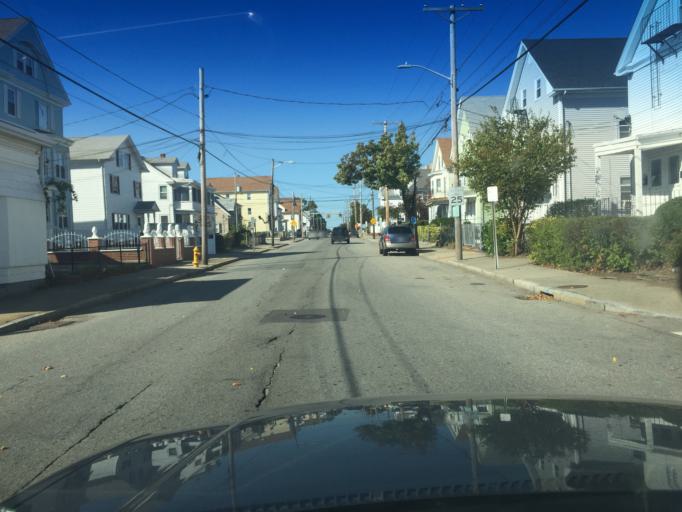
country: US
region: Rhode Island
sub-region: Providence County
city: Pawtucket
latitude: 41.8675
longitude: -71.3753
